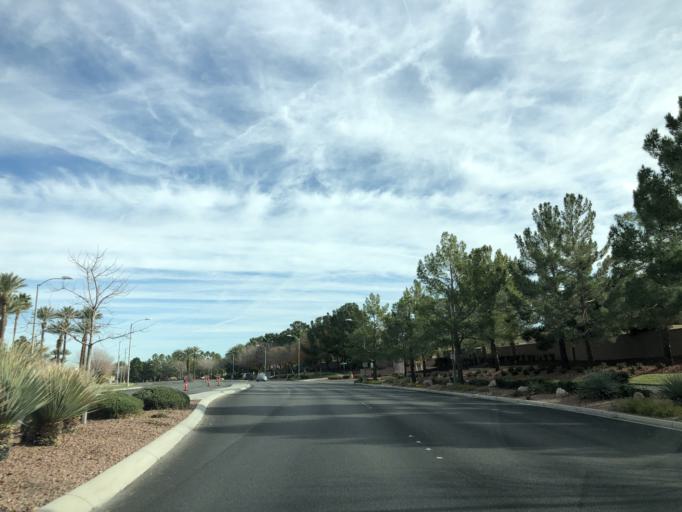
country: US
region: Nevada
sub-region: Clark County
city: Whitney
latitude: 36.0180
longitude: -115.0901
